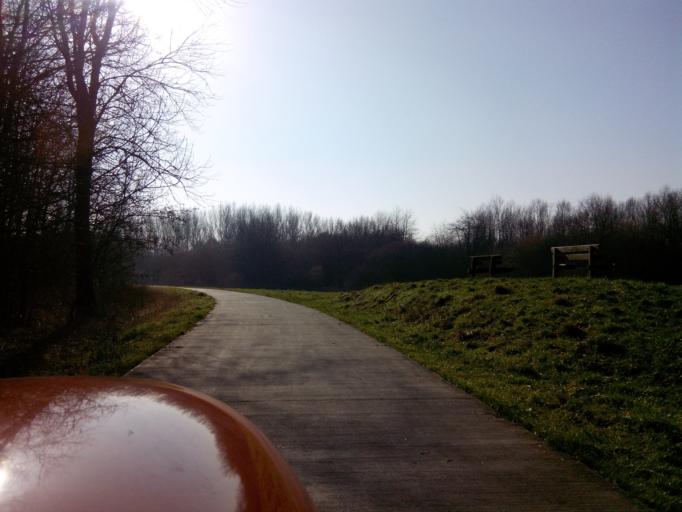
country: NL
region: Flevoland
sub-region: Gemeente Zeewolde
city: Zeewolde
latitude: 52.3297
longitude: 5.4810
